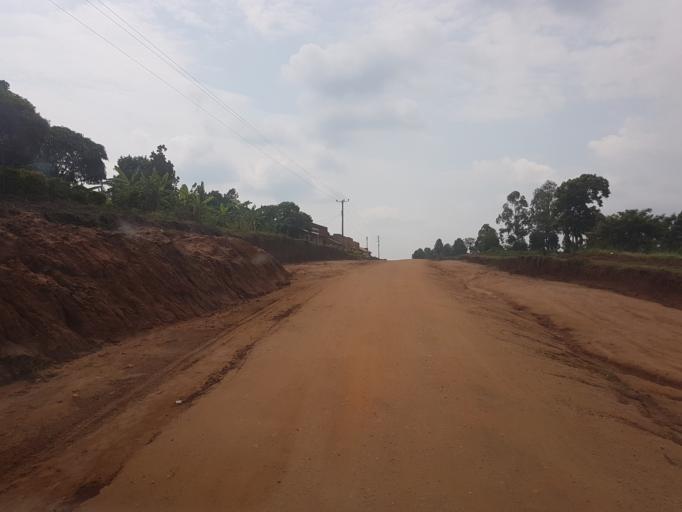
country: UG
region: Western Region
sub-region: Kanungu District
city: Ntungamo
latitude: -0.8164
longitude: 29.7064
